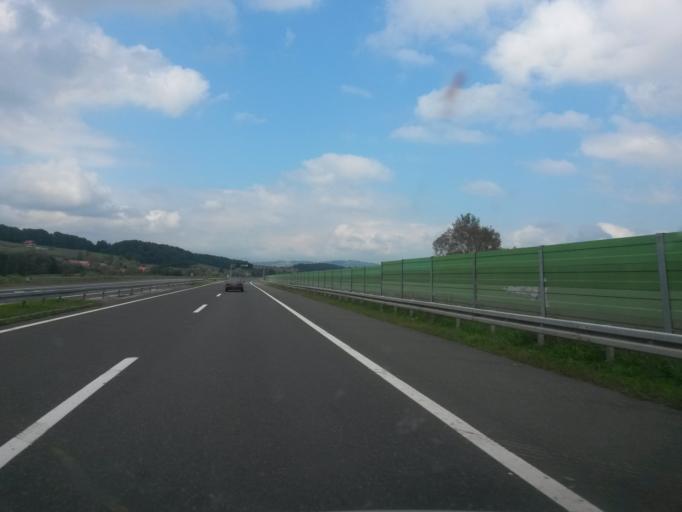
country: HR
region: Varazdinska
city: Remetinec
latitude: 46.0785
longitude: 16.2913
